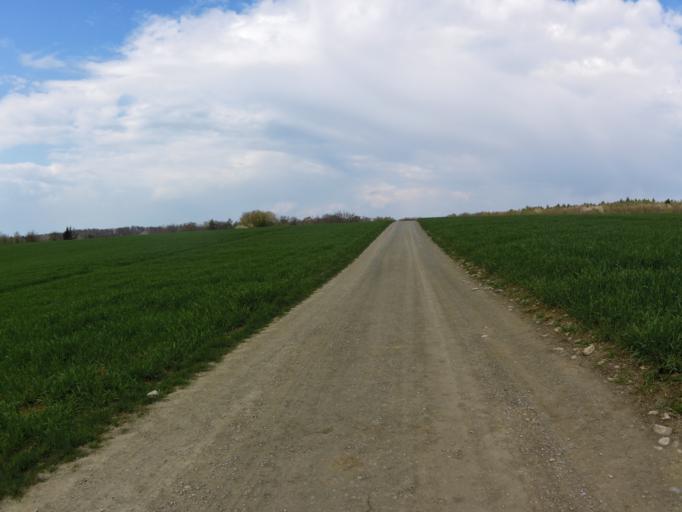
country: DE
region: Bavaria
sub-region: Regierungsbezirk Unterfranken
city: Rimpar
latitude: 49.8667
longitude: 9.9480
